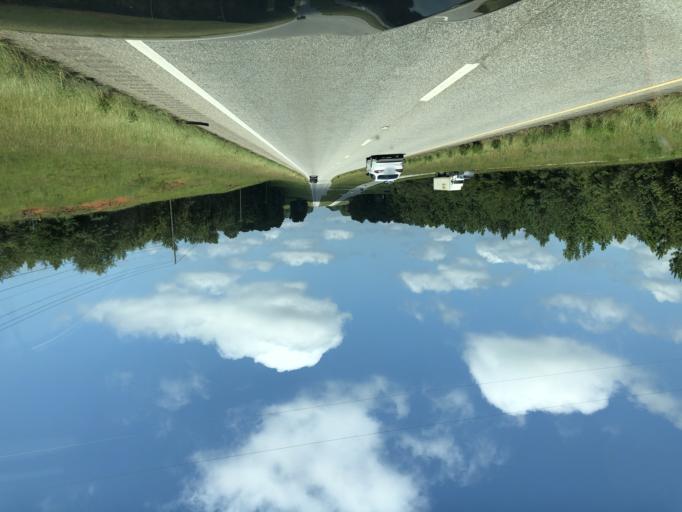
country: US
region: Alabama
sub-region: Henry County
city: Abbeville
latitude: 31.5656
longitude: -85.2808
